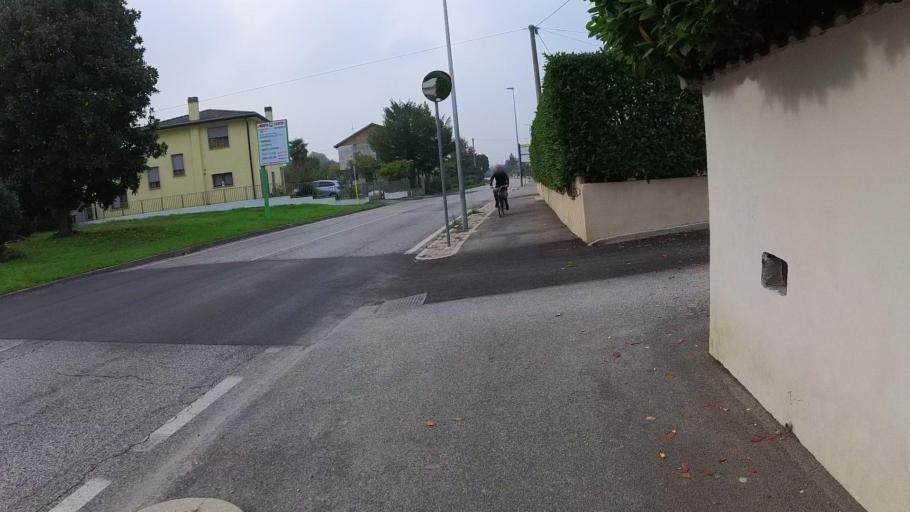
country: IT
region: Veneto
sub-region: Provincia di Venezia
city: Fosso
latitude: 45.3832
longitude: 12.0575
